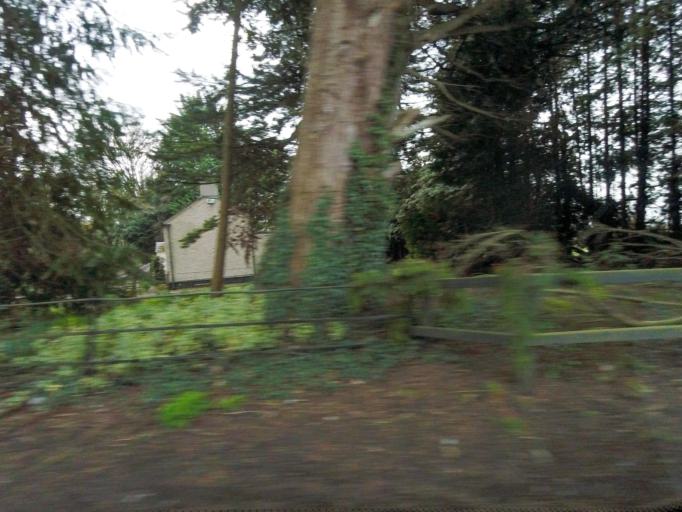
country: IE
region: Leinster
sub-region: Kildare
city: Eadestown
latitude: 53.1691
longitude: -6.6171
